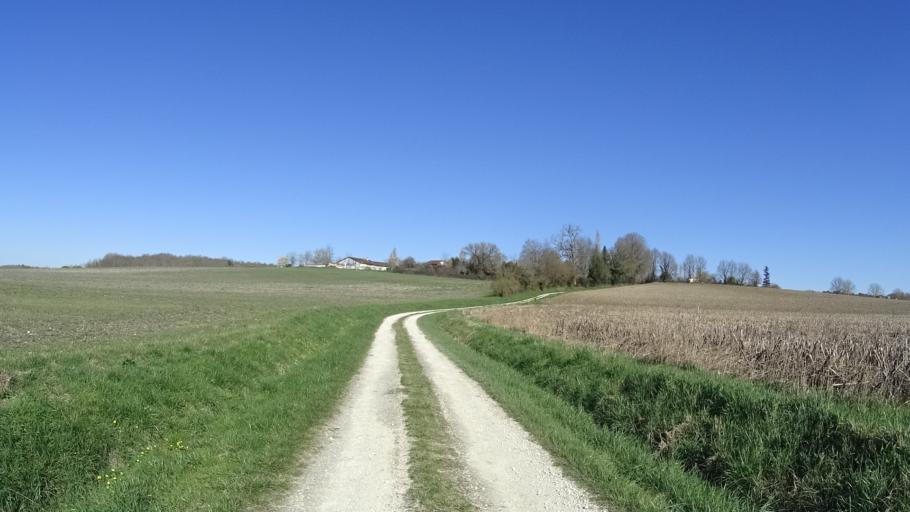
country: FR
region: Aquitaine
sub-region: Departement de la Dordogne
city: Saint-Aulaye
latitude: 45.2192
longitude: 0.1158
